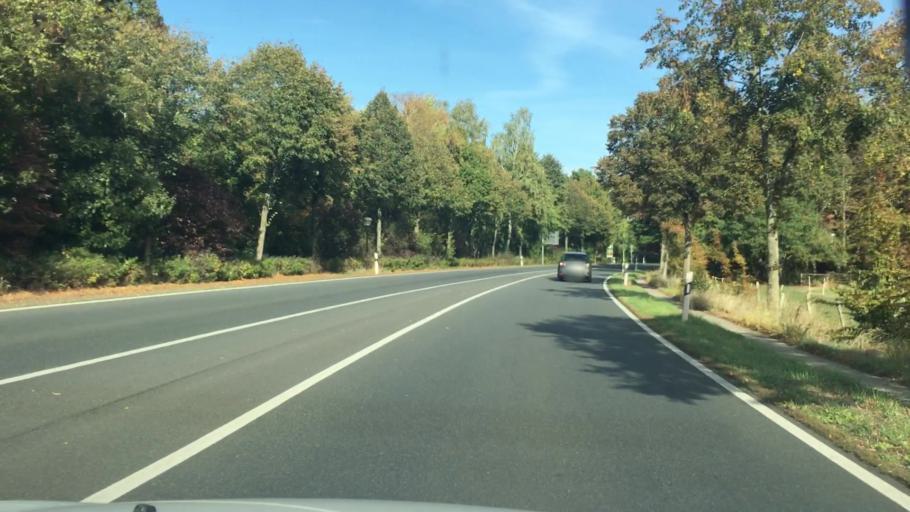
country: DE
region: Lower Saxony
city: Wehrbleck
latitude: 52.6323
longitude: 8.6917
